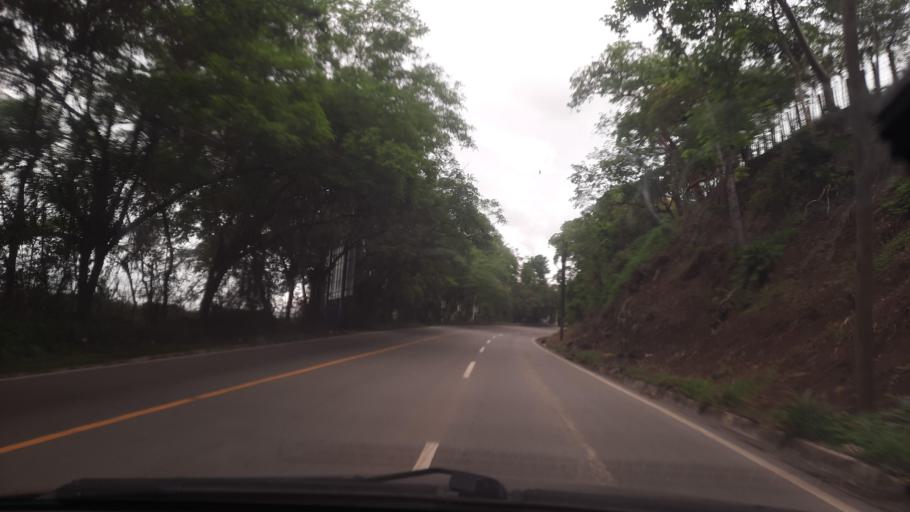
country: GT
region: Izabal
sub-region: Municipio de Los Amates
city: Los Amates
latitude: 15.2530
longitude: -89.1097
